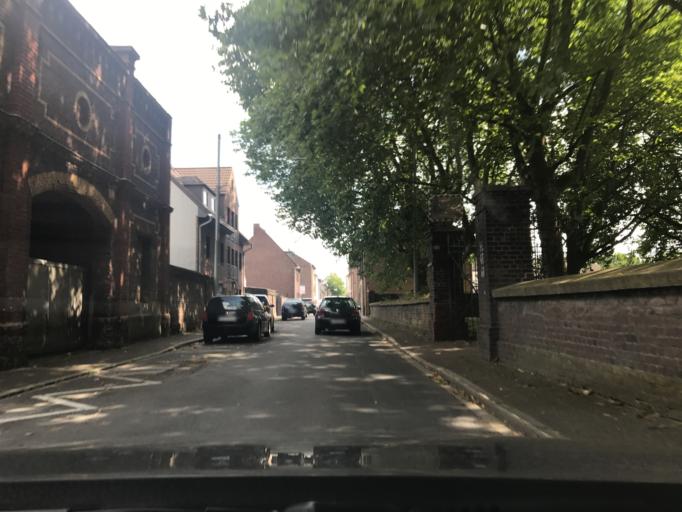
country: DE
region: North Rhine-Westphalia
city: Tonisvorst
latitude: 51.3709
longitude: 6.5103
